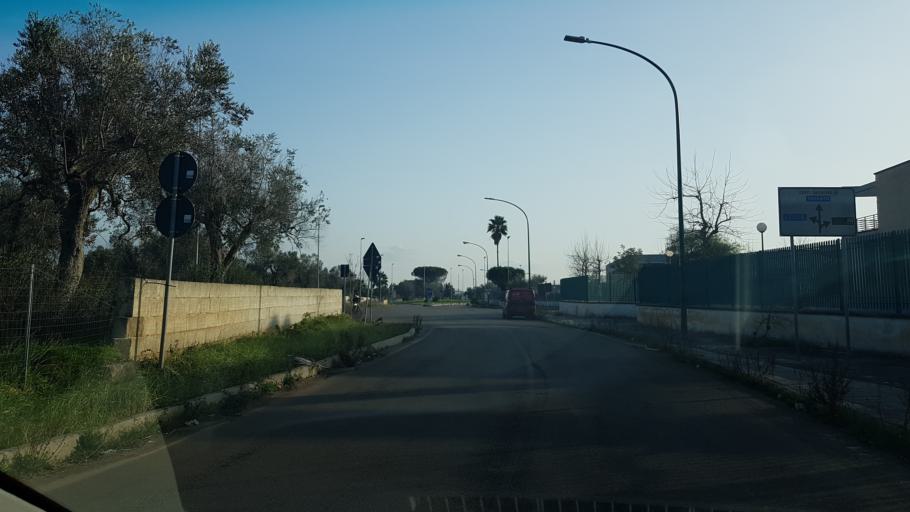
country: IT
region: Apulia
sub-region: Provincia di Lecce
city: Novoli
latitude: 40.3971
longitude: 18.0465
